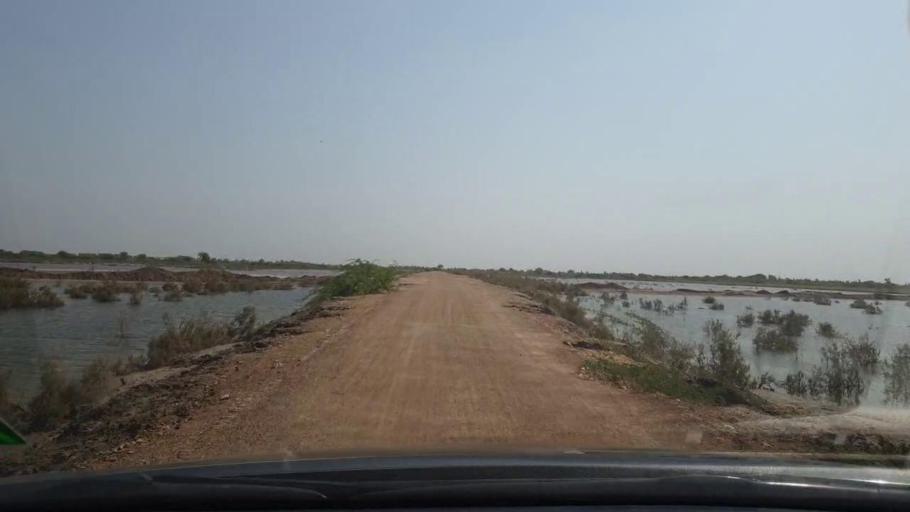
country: PK
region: Sindh
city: Tando Bago
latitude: 24.7937
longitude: 69.0867
